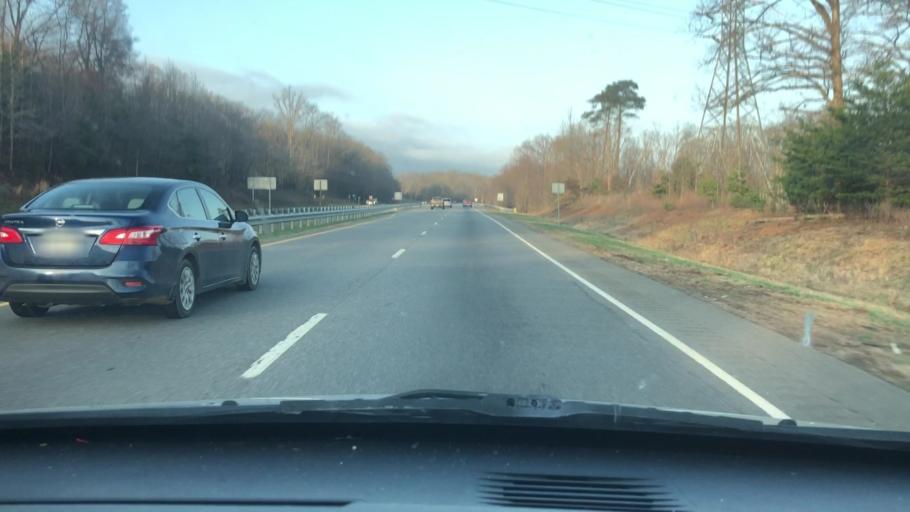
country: US
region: North Carolina
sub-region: Rockingham County
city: Mayodan
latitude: 36.4238
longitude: -79.9343
